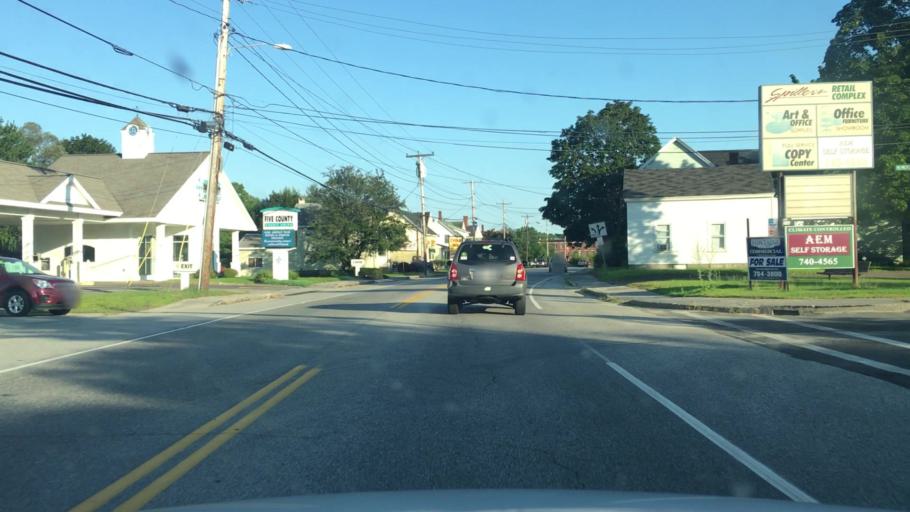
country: US
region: Maine
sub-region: Androscoggin County
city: Lisbon
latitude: 44.0335
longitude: -70.1058
